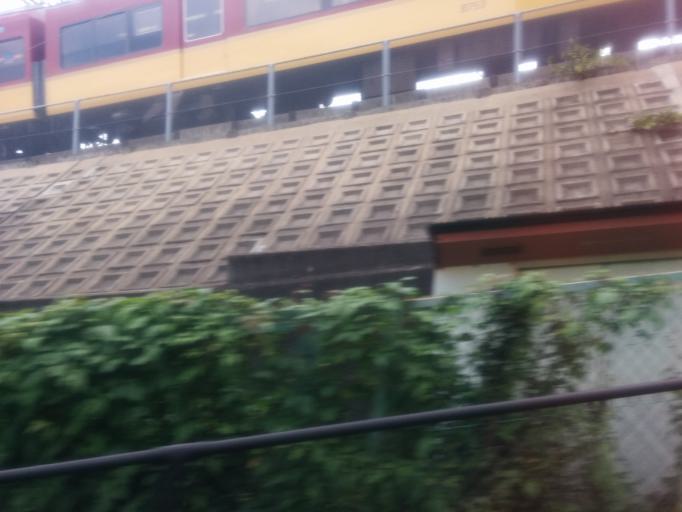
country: JP
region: Kyoto
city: Kyoto
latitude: 34.9786
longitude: 135.7701
